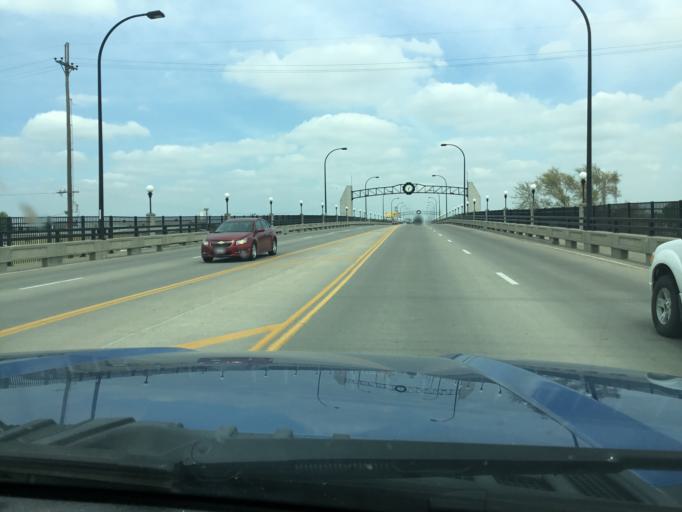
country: US
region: Kansas
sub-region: Shawnee County
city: Topeka
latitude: 39.0613
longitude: -95.6755
